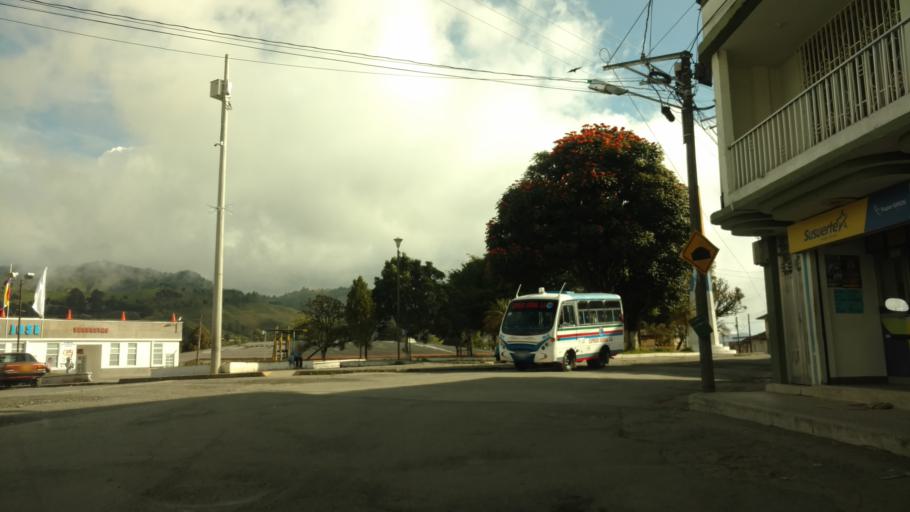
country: CO
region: Caldas
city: Aguadas
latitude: 5.6062
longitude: -75.4524
